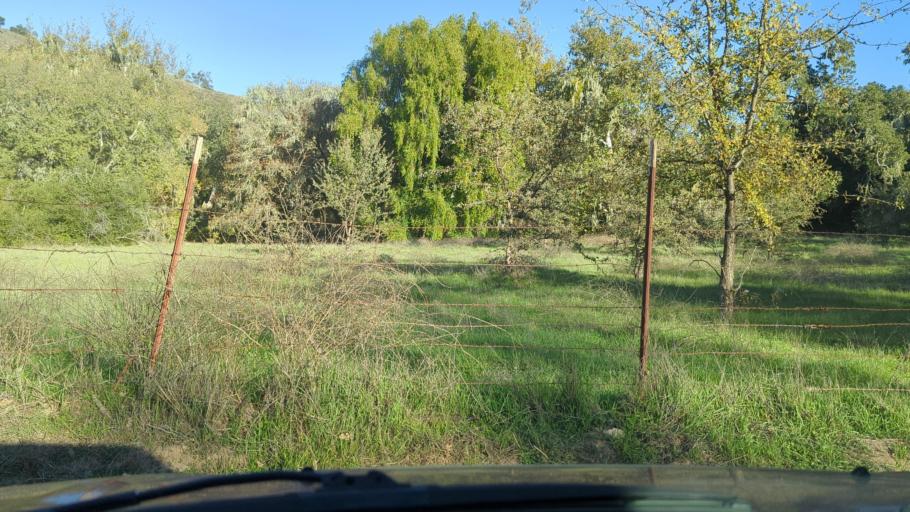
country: US
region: California
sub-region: Santa Barbara County
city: Santa Ynez
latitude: 34.5540
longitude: -120.0814
